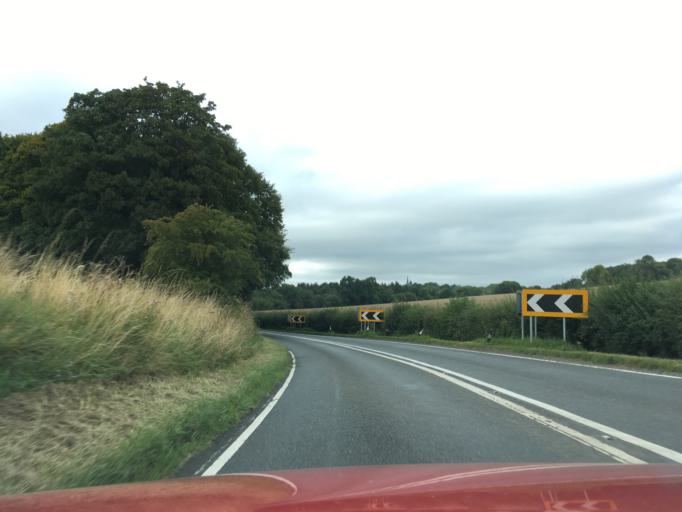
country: GB
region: England
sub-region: Hampshire
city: Four Marks
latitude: 51.0262
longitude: -1.0272
